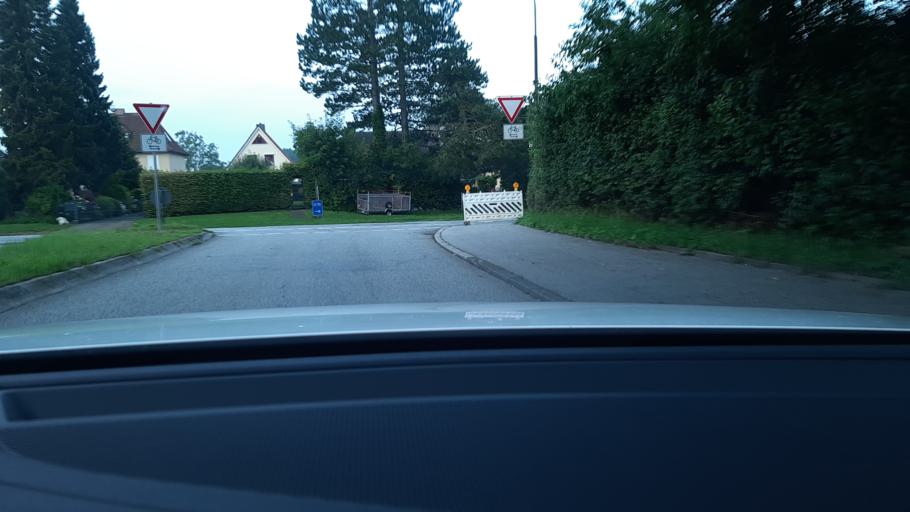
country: DE
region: Schleswig-Holstein
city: Stockelsdorf
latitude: 53.8511
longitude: 10.6318
